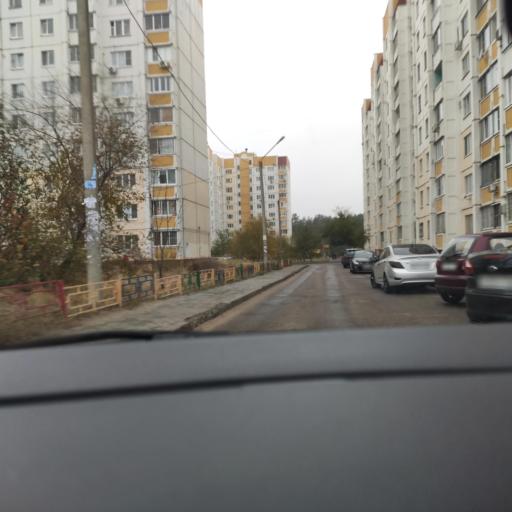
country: RU
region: Voronezj
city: Pridonskoy
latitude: 51.6580
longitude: 39.1007
